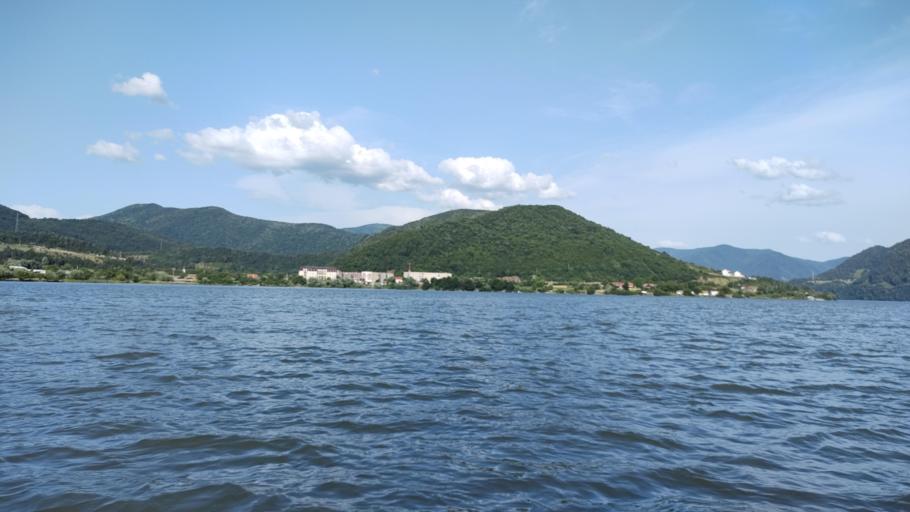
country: RO
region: Caras-Severin
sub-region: Comuna Berzasca
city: Berzasca
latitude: 44.6438
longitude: 21.9410
